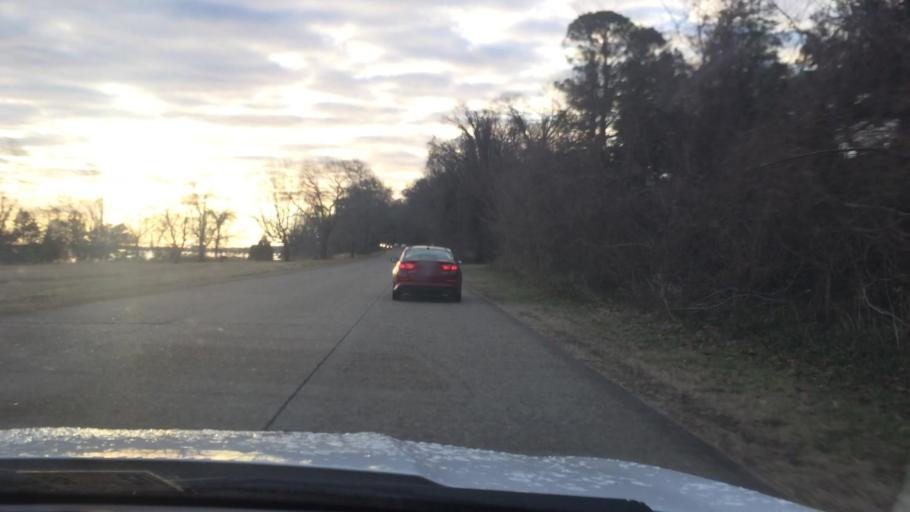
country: US
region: Virginia
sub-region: York County
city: Yorktown
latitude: 37.2627
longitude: -76.5502
